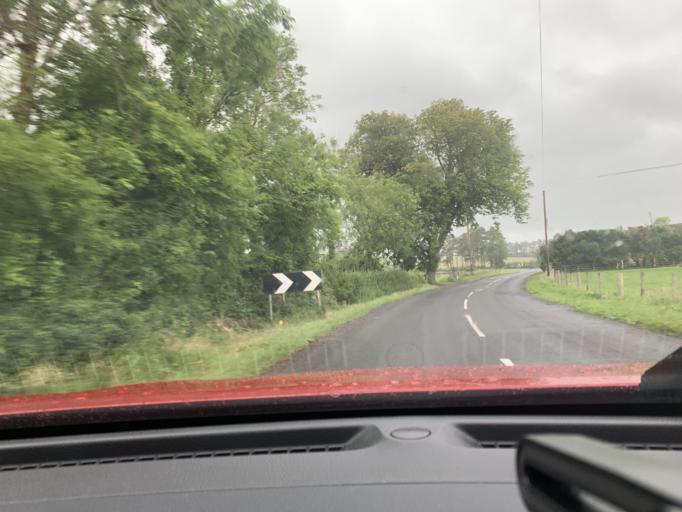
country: GB
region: Northern Ireland
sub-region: Fermanagh District
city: Enniskillen
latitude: 54.3086
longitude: -7.6857
